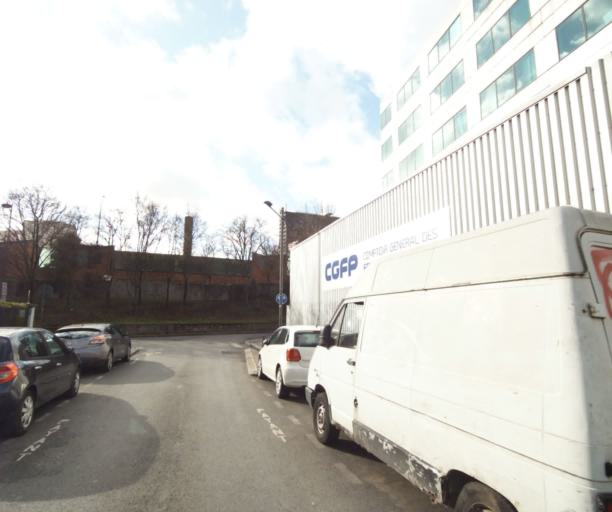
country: FR
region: Ile-de-France
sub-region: Paris
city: Saint-Ouen
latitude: 48.9016
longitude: 2.3481
